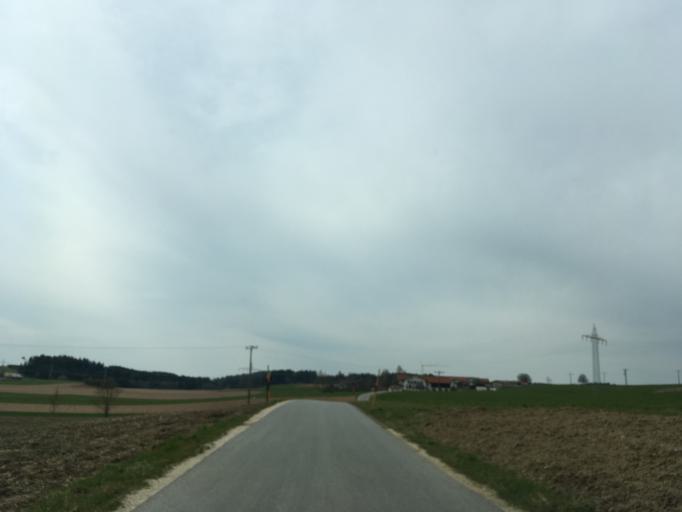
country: DE
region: Bavaria
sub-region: Upper Bavaria
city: Hoslwang
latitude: 47.9782
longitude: 12.3510
